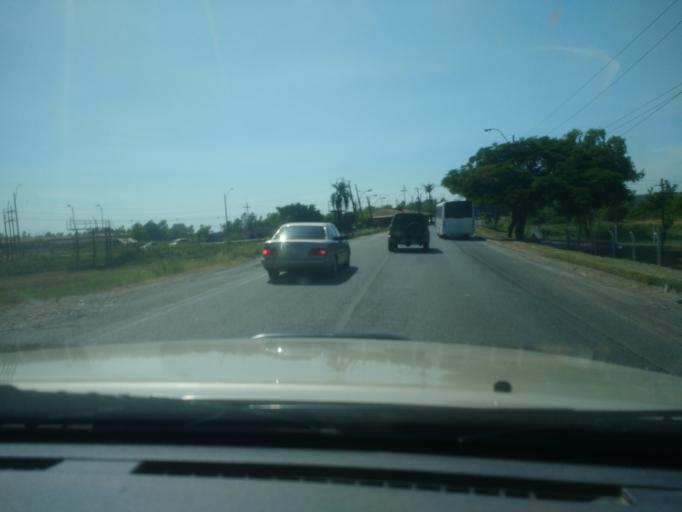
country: PY
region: Central
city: Colonia Mariano Roque Alonso
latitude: -25.1721
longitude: -57.5616
